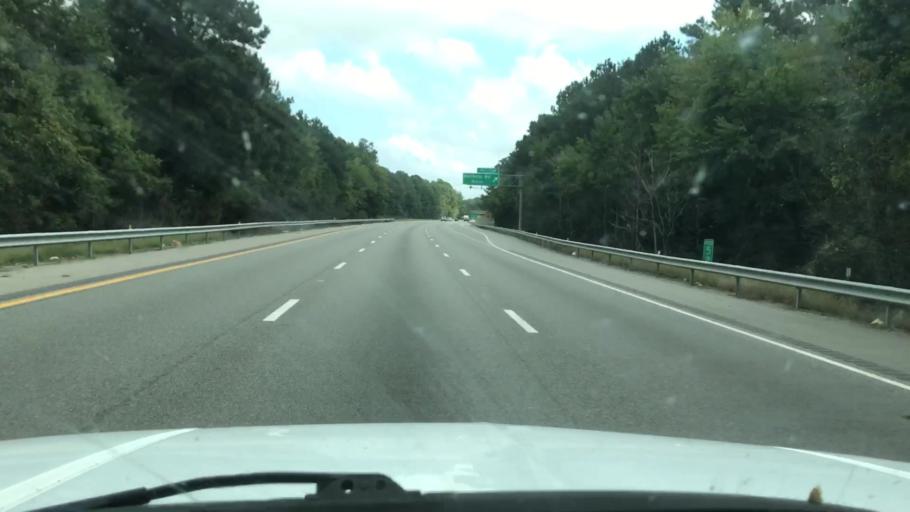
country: US
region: Virginia
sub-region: Henrico County
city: Short Pump
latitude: 37.6668
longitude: -77.5908
